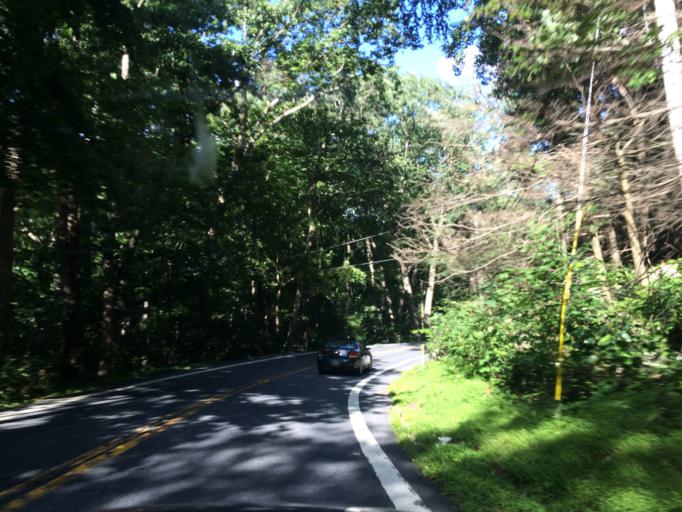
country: US
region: Maryland
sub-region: Frederick County
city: Thurmont
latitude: 39.6209
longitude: -77.4352
